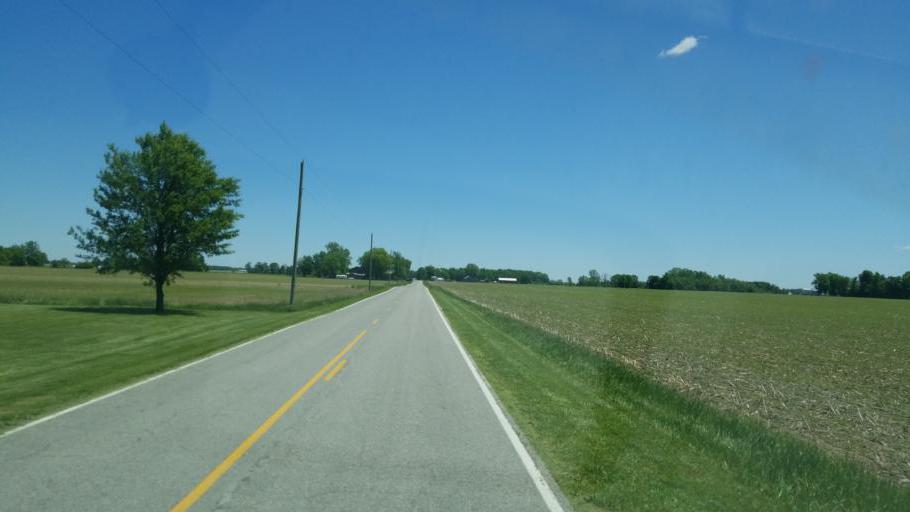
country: US
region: Indiana
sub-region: Randolph County
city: Union City
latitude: 40.2817
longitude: -84.7748
